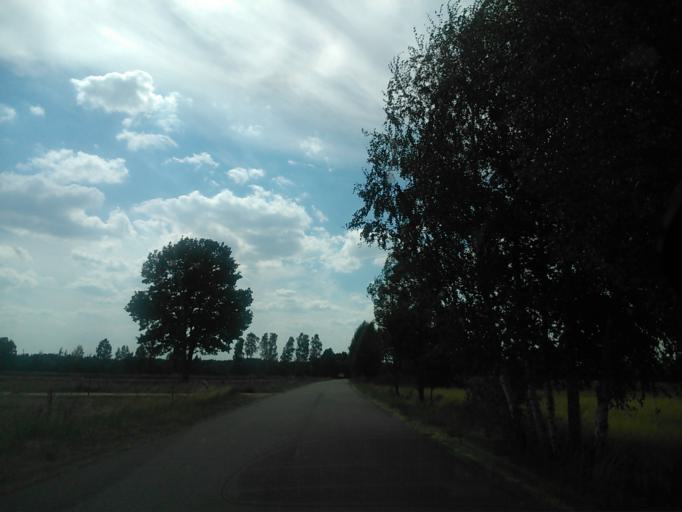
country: PL
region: Masovian Voivodeship
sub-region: Powiat ostrolecki
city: Czarnia
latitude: 53.3676
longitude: 21.1972
